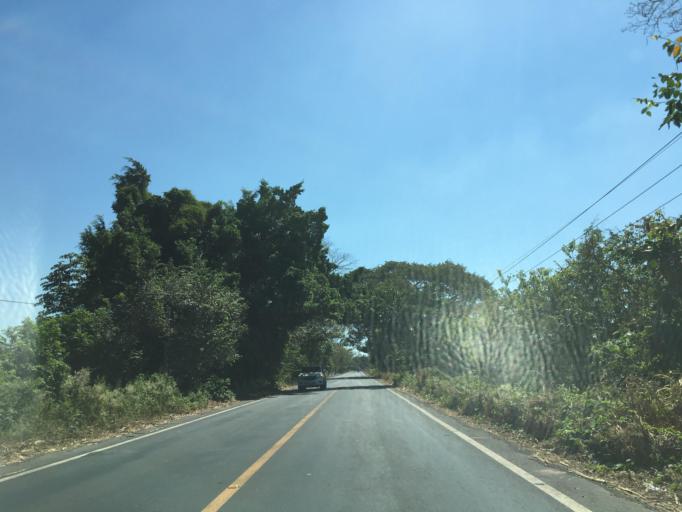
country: GT
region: Escuintla
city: Puerto San Jose
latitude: 13.9791
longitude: -90.8853
